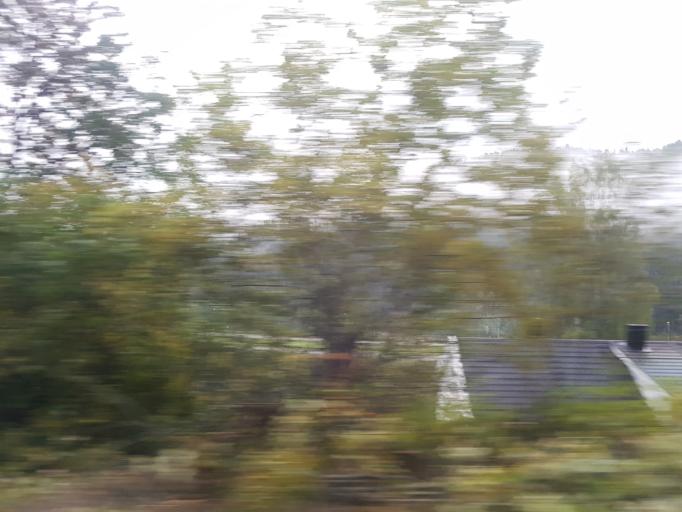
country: NO
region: Sor-Trondelag
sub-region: Midtre Gauldal
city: Storen
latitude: 63.0293
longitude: 10.2642
